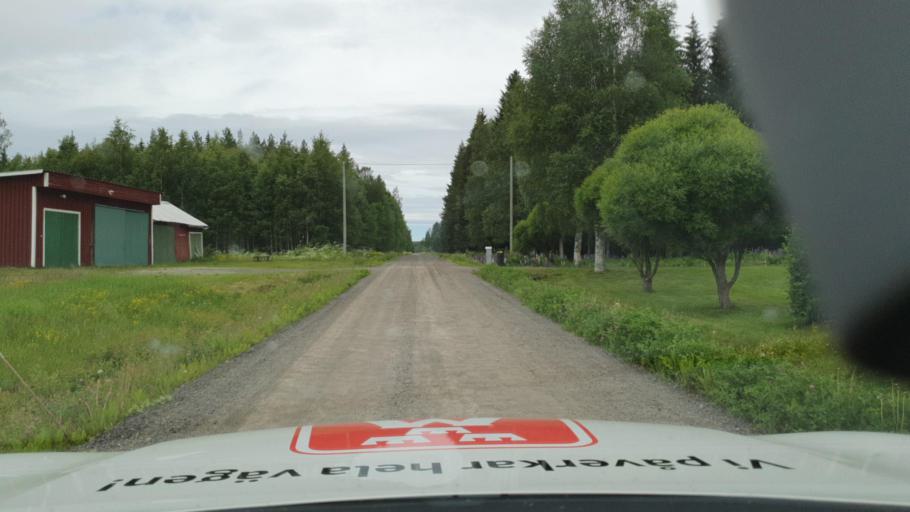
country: SE
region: Vaesterbotten
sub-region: Skelleftea Kommun
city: Burtraesk
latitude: 64.3975
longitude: 20.5740
